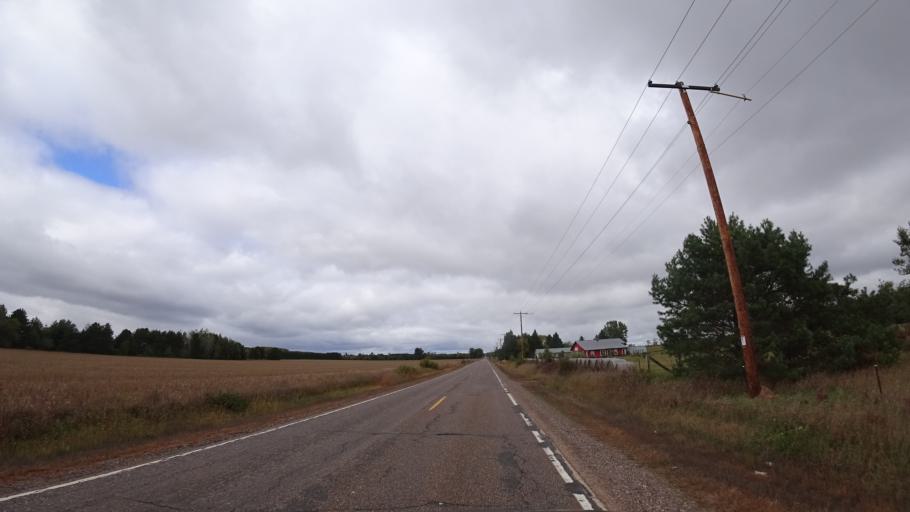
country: US
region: Wisconsin
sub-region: Chippewa County
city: Lake Wissota
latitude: 44.9635
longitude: -91.2678
